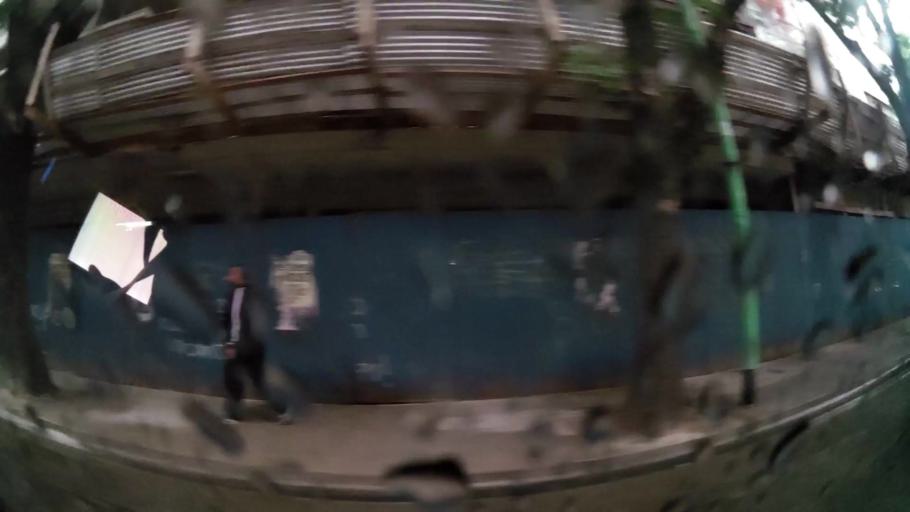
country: AR
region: Buenos Aires
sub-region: Partido de Avellaneda
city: Avellaneda
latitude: -34.6382
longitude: -58.3639
